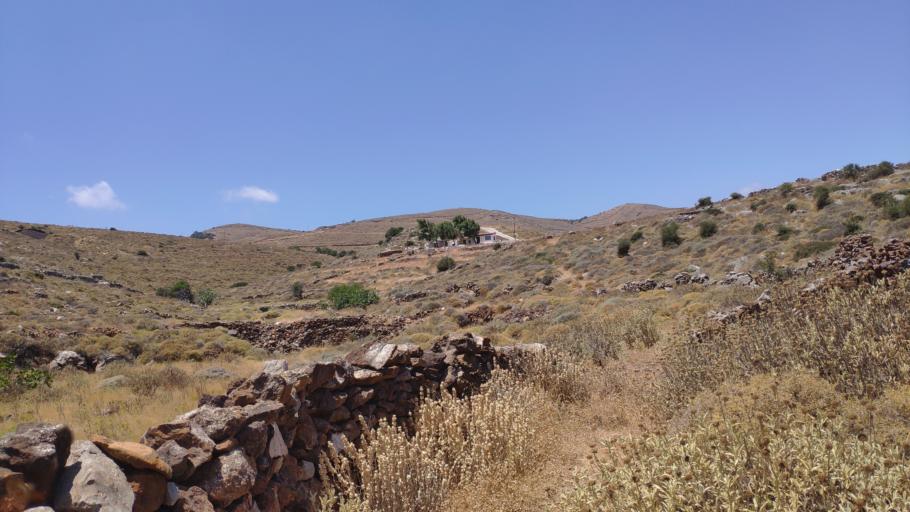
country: GR
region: South Aegean
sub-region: Nomos Kykladon
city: Kythnos
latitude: 37.3797
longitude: 24.4549
